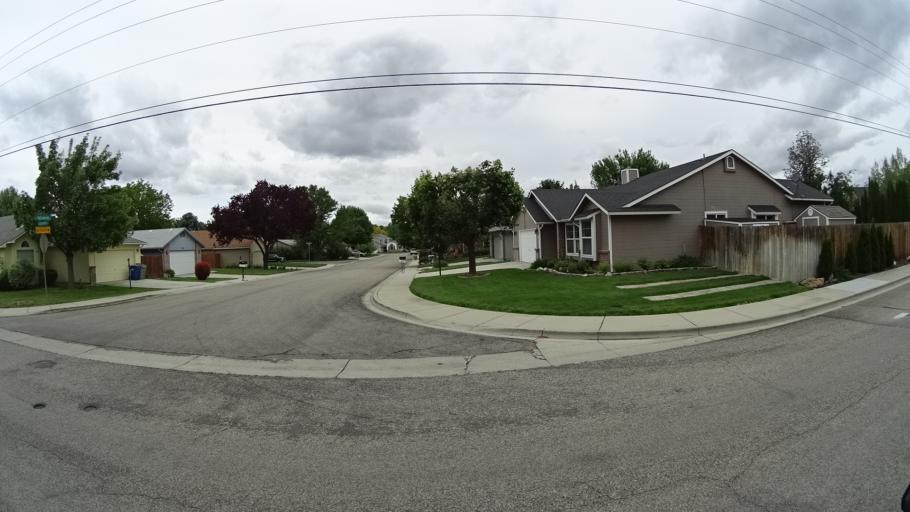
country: US
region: Idaho
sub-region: Ada County
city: Eagle
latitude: 43.6989
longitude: -116.3341
